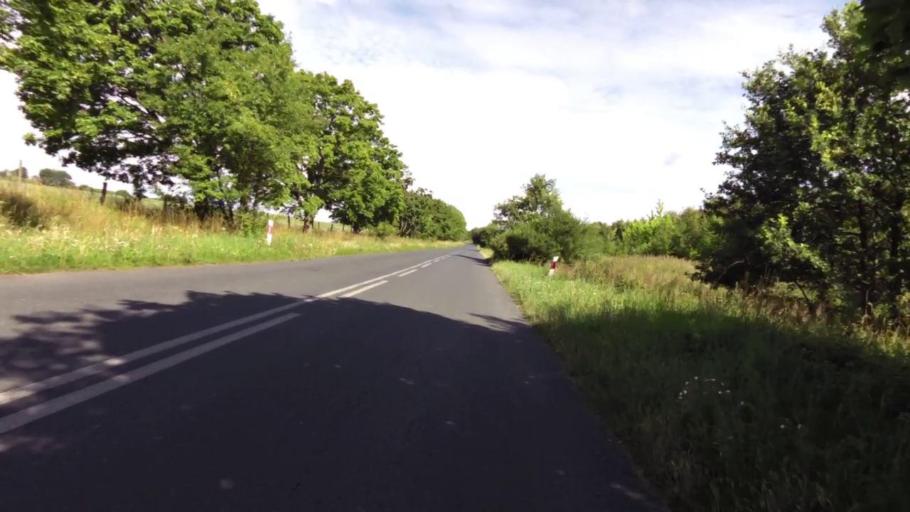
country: PL
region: West Pomeranian Voivodeship
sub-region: Powiat stargardzki
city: Dobrzany
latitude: 53.3902
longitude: 15.4336
